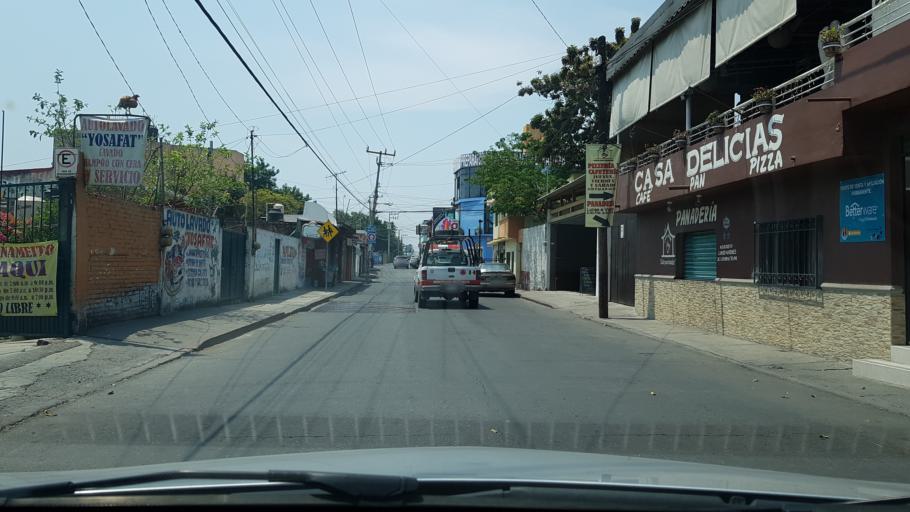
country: MX
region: Morelos
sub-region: Jiutepec
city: Jiutepec
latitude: 18.8847
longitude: -99.1772
